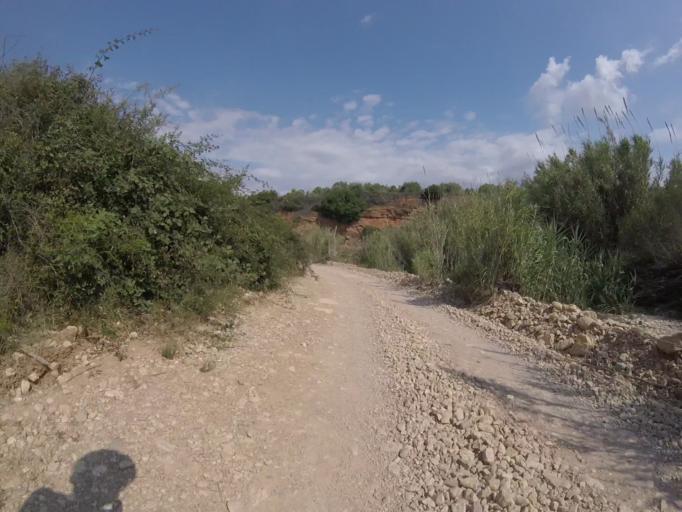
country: ES
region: Valencia
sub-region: Provincia de Castello
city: Cuevas de Vinroma
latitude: 40.3091
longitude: 0.1736
